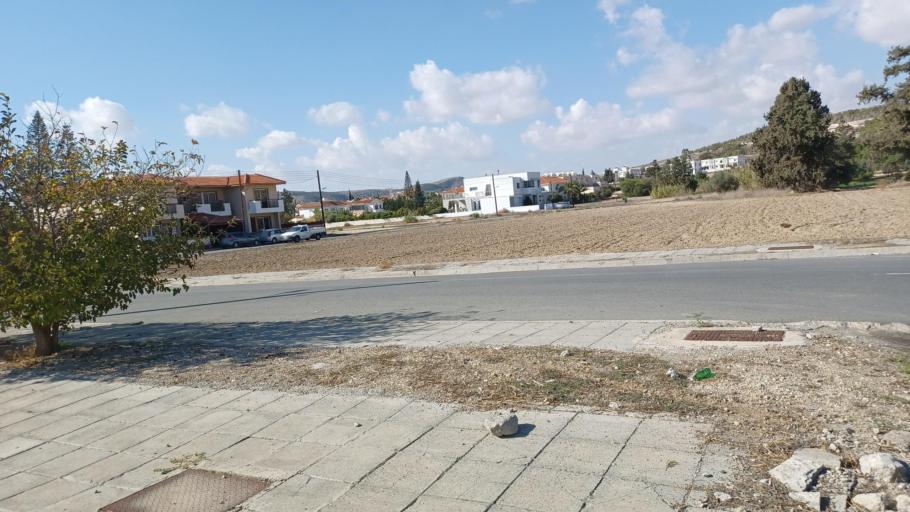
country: CY
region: Larnaka
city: Pyla
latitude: 34.9981
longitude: 33.6862
